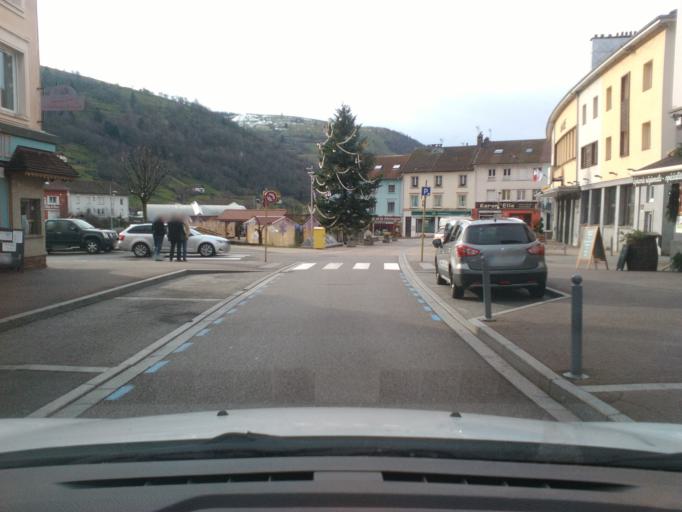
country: FR
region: Lorraine
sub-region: Departement des Vosges
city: La Bresse
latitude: 48.0041
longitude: 6.8743
